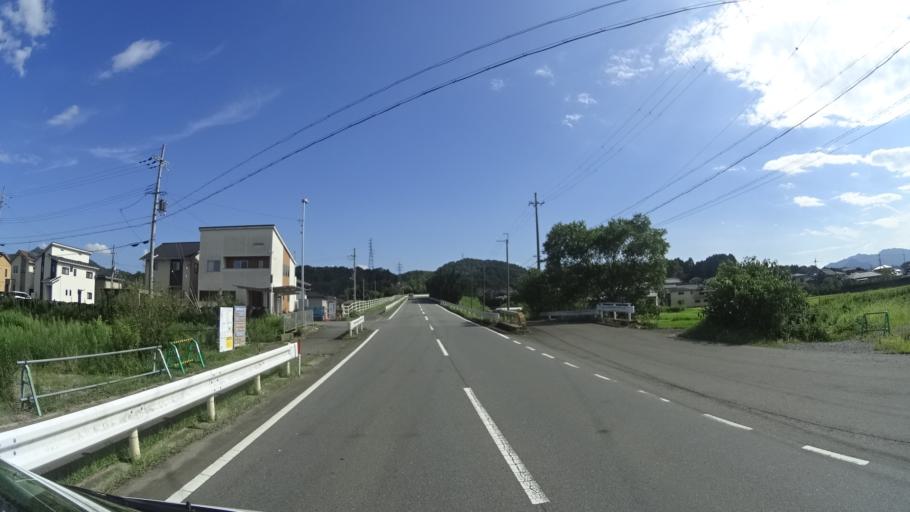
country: JP
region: Kyoto
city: Fukuchiyama
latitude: 35.3016
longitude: 135.1708
